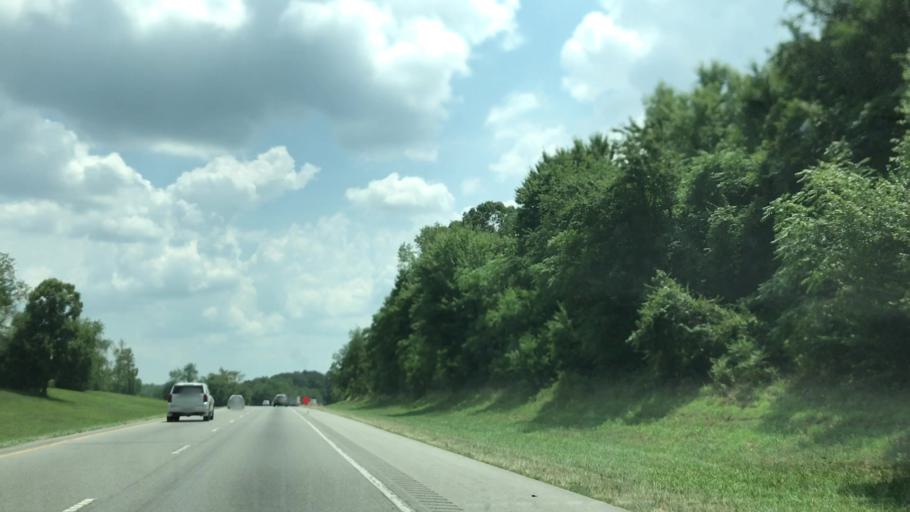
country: US
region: North Carolina
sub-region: Iredell County
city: Statesville
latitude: 35.9829
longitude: -80.8391
